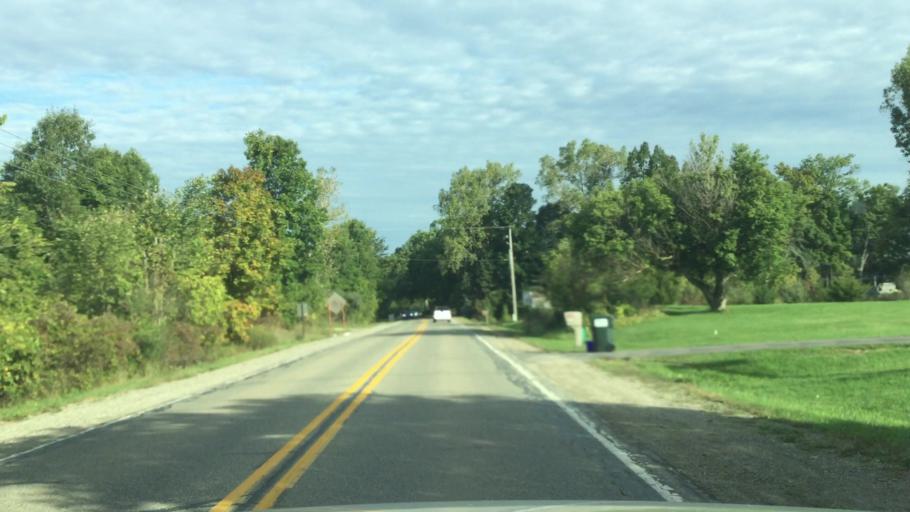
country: US
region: Michigan
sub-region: Livingston County
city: Howell
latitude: 42.5906
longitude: -83.9009
